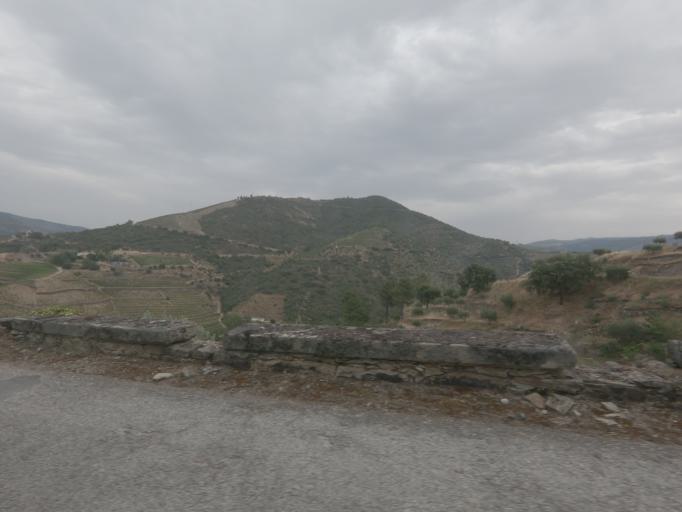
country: PT
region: Viseu
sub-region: Armamar
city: Armamar
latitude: 41.1506
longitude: -7.6444
